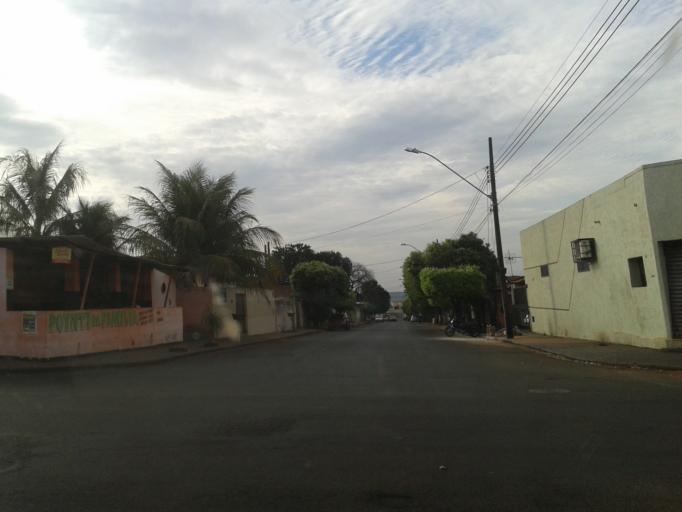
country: BR
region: Minas Gerais
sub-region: Ituiutaba
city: Ituiutaba
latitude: -18.9867
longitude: -49.4502
